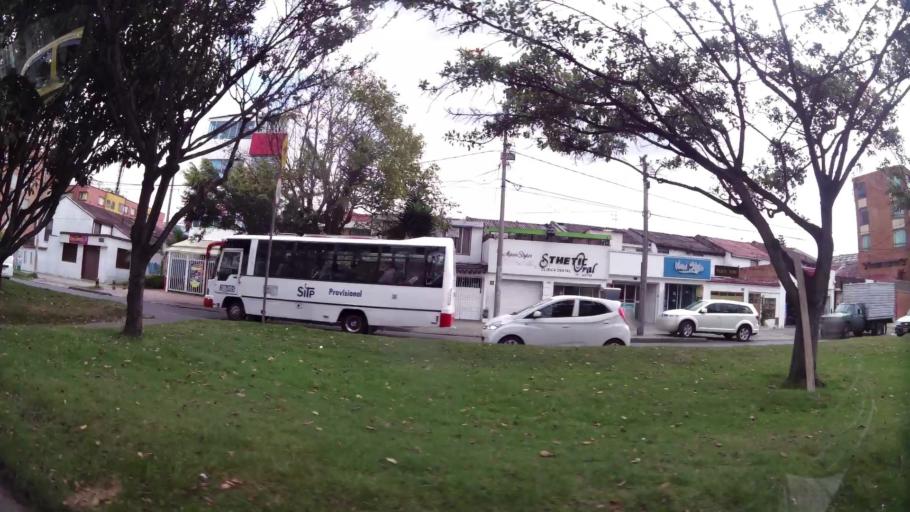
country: CO
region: Bogota D.C.
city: Bogota
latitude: 4.6099
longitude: -74.1092
